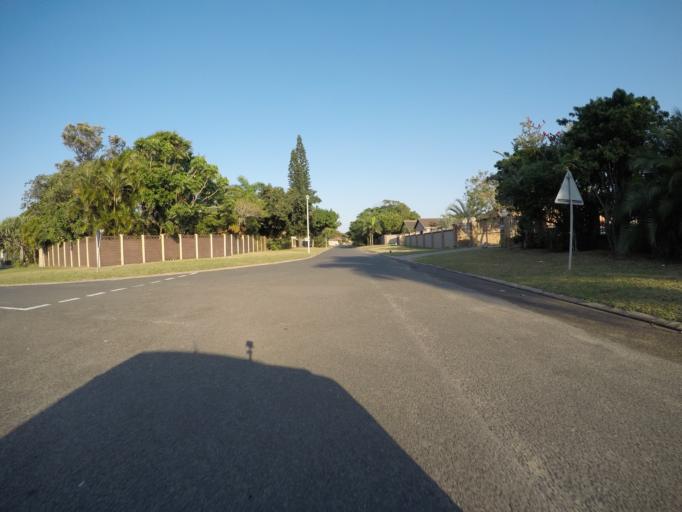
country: ZA
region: KwaZulu-Natal
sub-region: uThungulu District Municipality
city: Richards Bay
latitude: -28.7800
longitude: 32.1139
